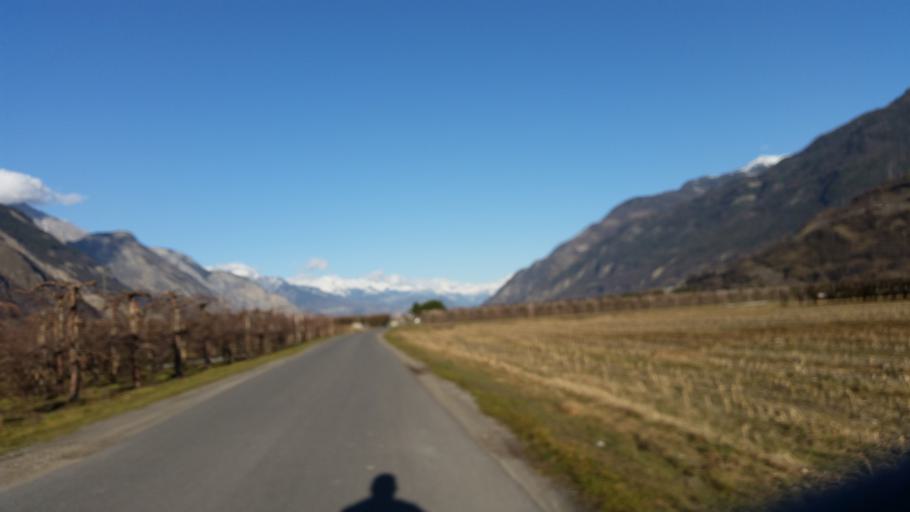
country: CH
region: Valais
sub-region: Martigny District
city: Charrat-les-Chenes
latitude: 46.1394
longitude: 7.1416
